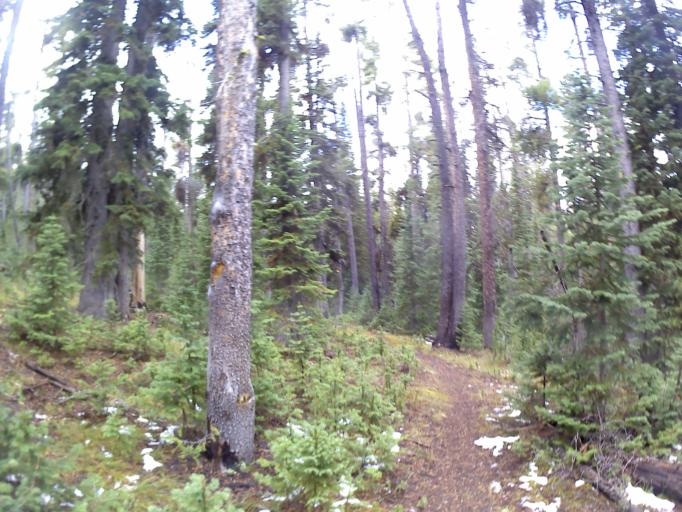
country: US
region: Montana
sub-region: Gallatin County
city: West Yellowstone
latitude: 44.4328
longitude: -110.7365
